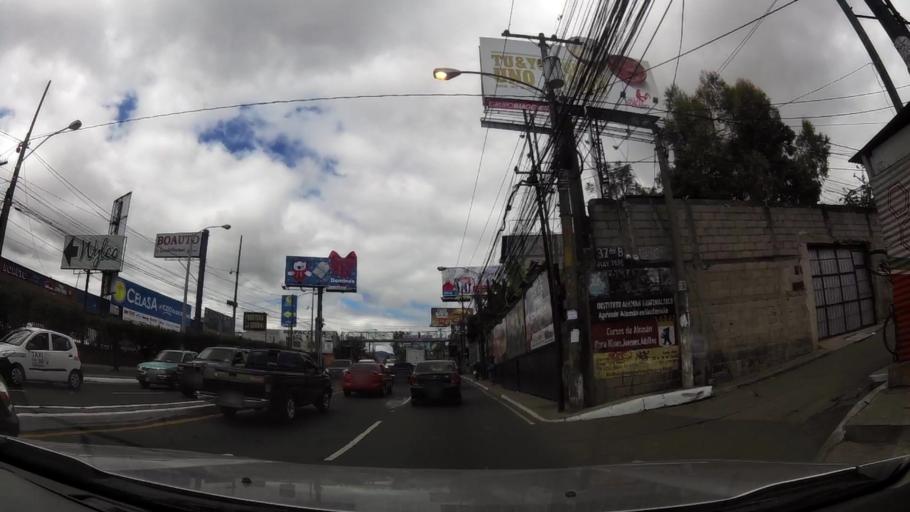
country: GT
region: Guatemala
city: Mixco
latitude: 14.6383
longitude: -90.5639
